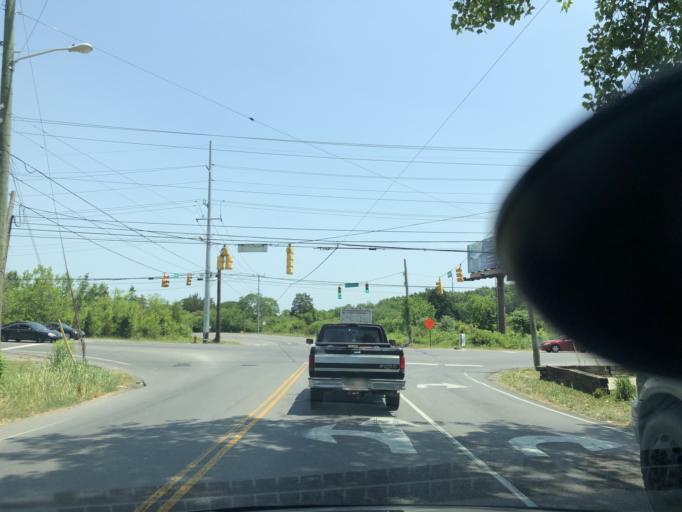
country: US
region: Tennessee
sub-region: Rutherford County
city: La Vergne
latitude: 36.0540
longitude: -86.6191
